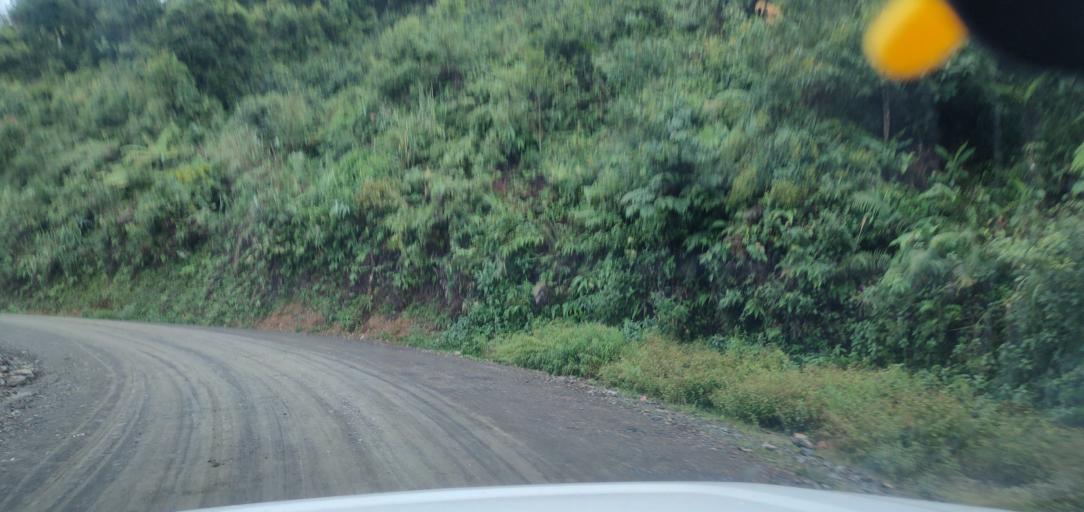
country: LA
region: Phongsali
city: Phongsali
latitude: 21.4288
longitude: 102.1657
